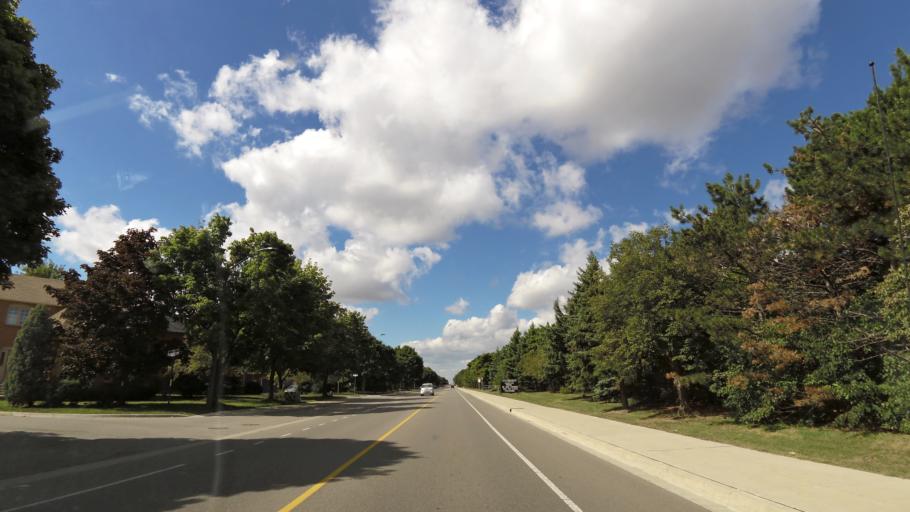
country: CA
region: Ontario
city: Mississauga
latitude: 43.5688
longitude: -79.7554
